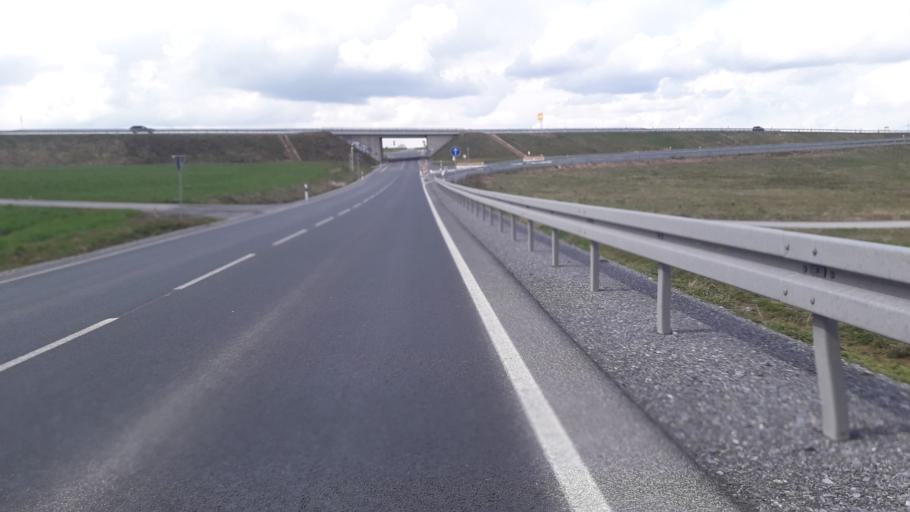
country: DE
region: North Rhine-Westphalia
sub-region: Regierungsbezirk Detmold
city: Wunnenberg
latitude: 51.4997
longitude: 8.6741
